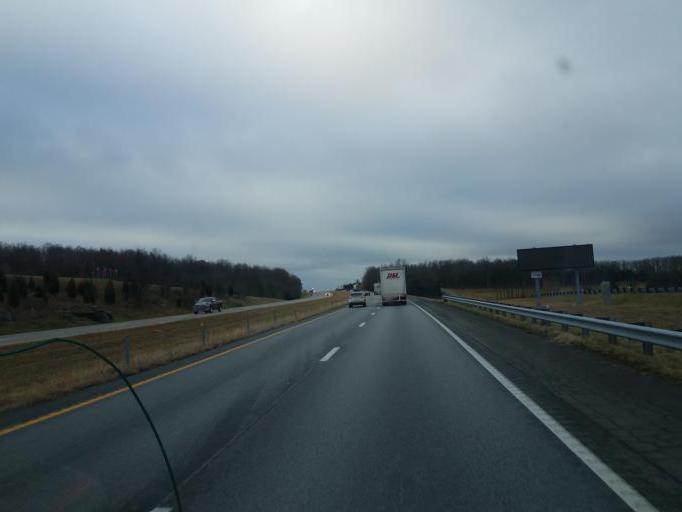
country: US
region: Missouri
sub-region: Webster County
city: Marshfield
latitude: 37.5263
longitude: -92.8298
